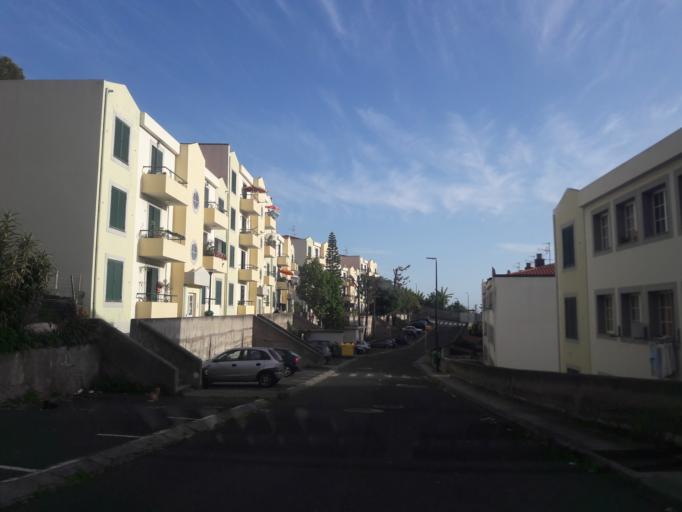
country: PT
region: Madeira
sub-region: Funchal
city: Nossa Senhora do Monte
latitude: 32.6570
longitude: -16.9292
